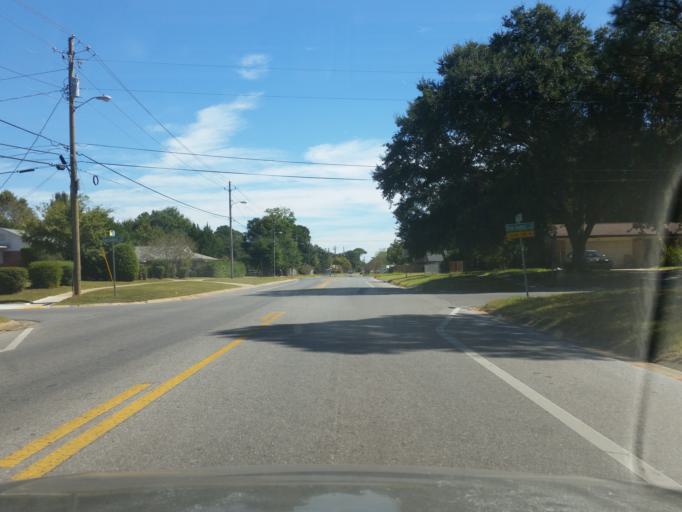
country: US
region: Florida
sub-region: Escambia County
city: Ferry Pass
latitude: 30.4866
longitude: -87.1770
